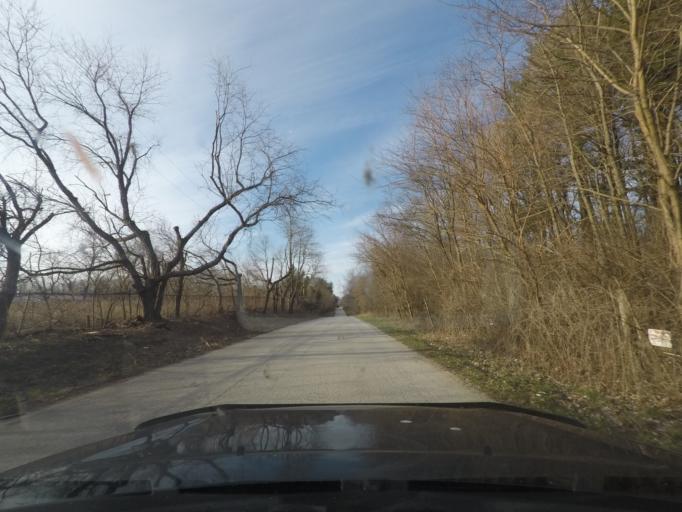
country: US
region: Indiana
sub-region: LaPorte County
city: Westville
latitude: 41.5181
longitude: -86.7988
